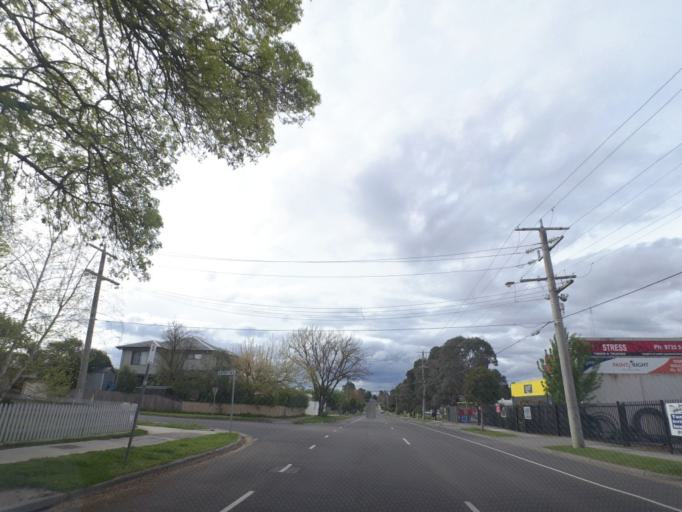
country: AU
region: Victoria
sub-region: Yarra Ranges
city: Lilydale
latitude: -37.7537
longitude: 145.3436
